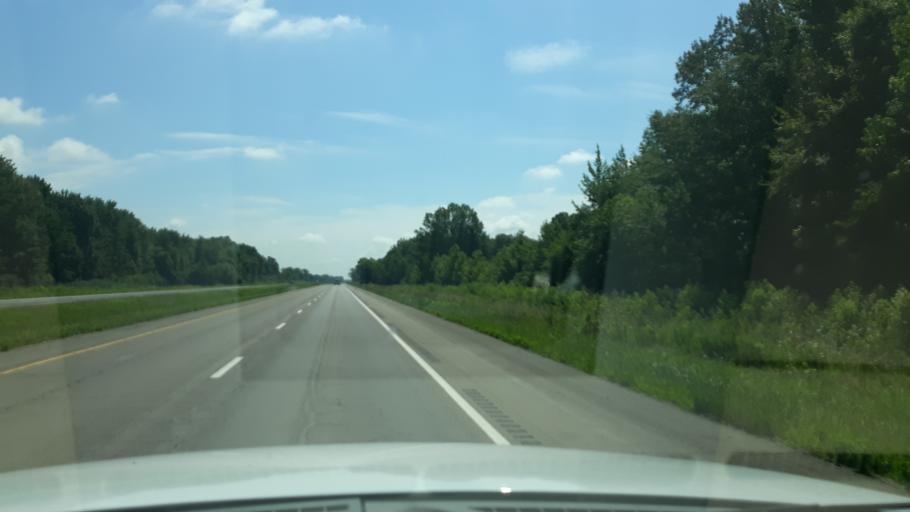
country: US
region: Illinois
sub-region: Saline County
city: Carrier Mills
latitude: 37.7333
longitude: -88.6644
